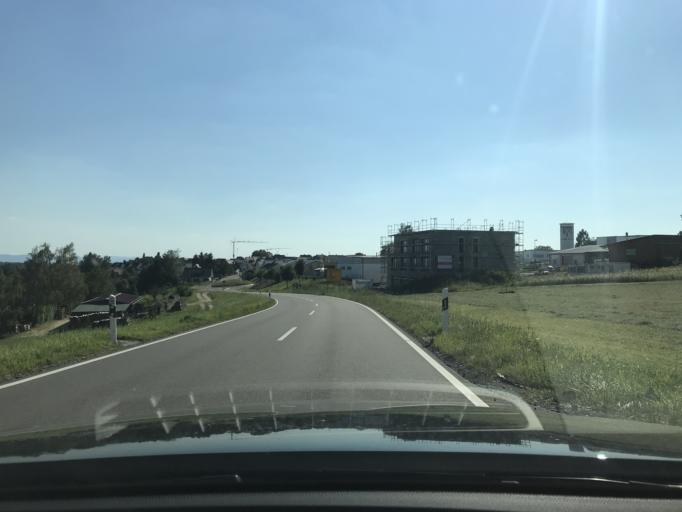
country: DE
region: Baden-Wuerttemberg
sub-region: Regierungsbezirk Stuttgart
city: Baltmannsweiler
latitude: 48.7559
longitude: 9.4877
